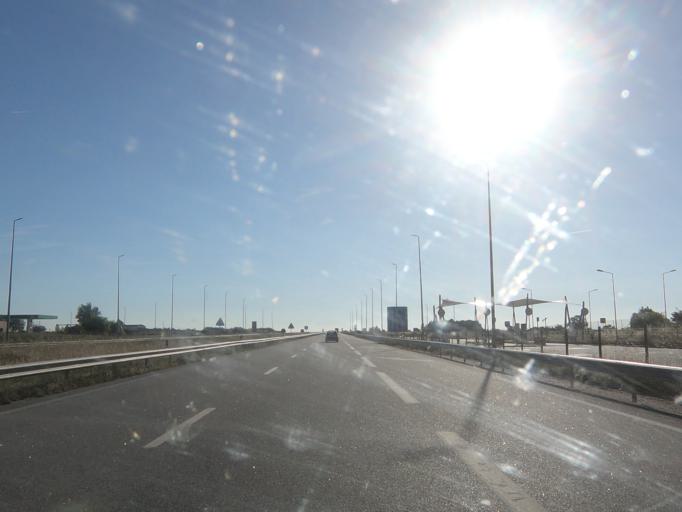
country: ES
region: Castille and Leon
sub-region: Provincia de Salamanca
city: Fuentes de Onoro
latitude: 40.6046
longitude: -6.9514
